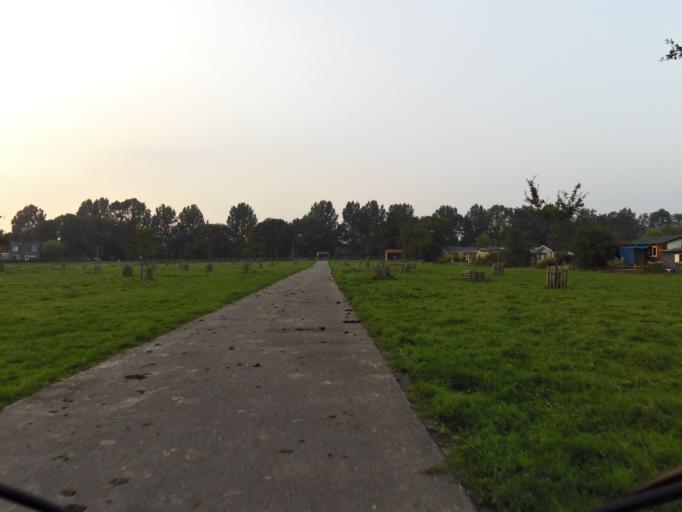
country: NL
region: South Holland
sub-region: Gemeente Voorschoten
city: Voorschoten
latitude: 52.1342
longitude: 4.4764
